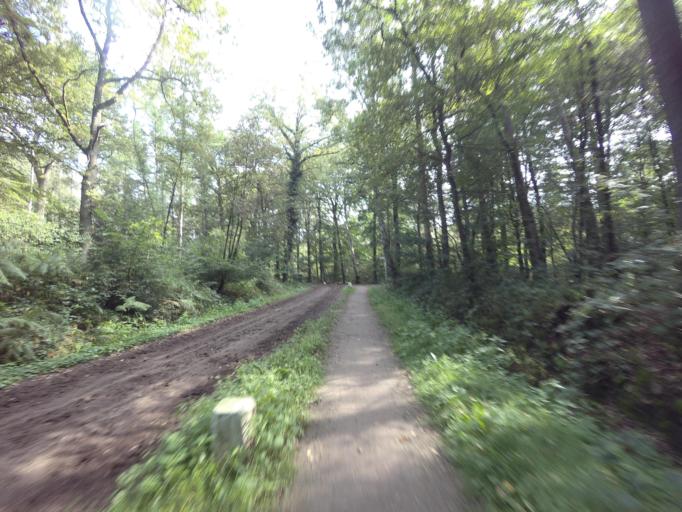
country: NL
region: Overijssel
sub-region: Gemeente Hengelo
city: Hengelo
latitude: 52.2594
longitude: 6.8502
